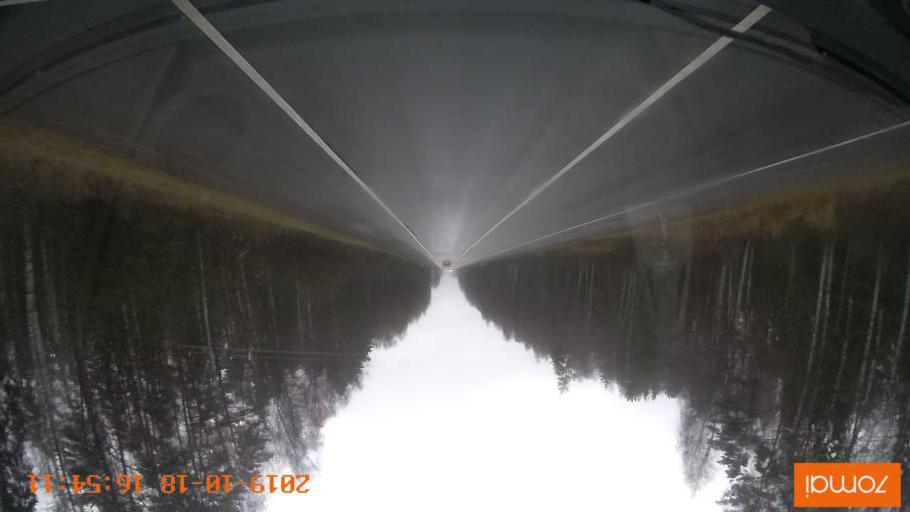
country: RU
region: Ivanovo
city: Nerl'
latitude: 56.6261
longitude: 40.5676
